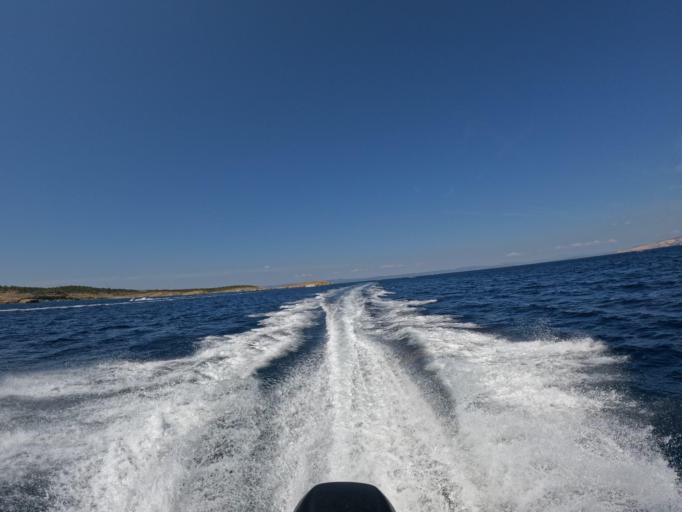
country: HR
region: Primorsko-Goranska
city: Lopar
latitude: 44.8533
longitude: 14.7382
